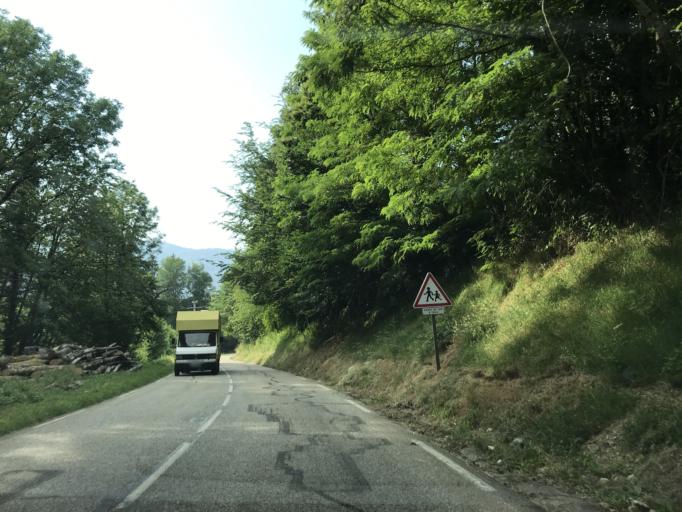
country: FR
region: Rhone-Alpes
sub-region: Departement de l'Isere
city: Allevard
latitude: 45.3824
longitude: 6.0868
